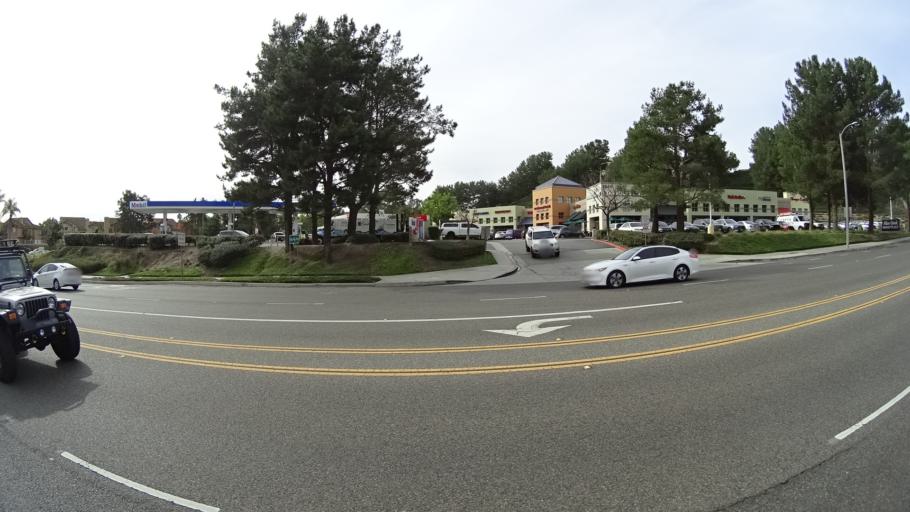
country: US
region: California
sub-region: Orange County
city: Laguna Woods
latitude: 33.5882
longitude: -117.7209
